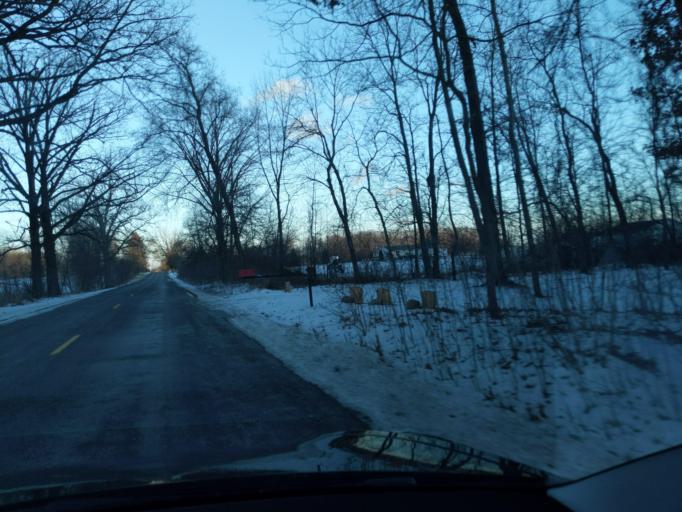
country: US
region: Michigan
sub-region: Ingham County
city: Stockbridge
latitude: 42.4613
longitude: -84.2348
